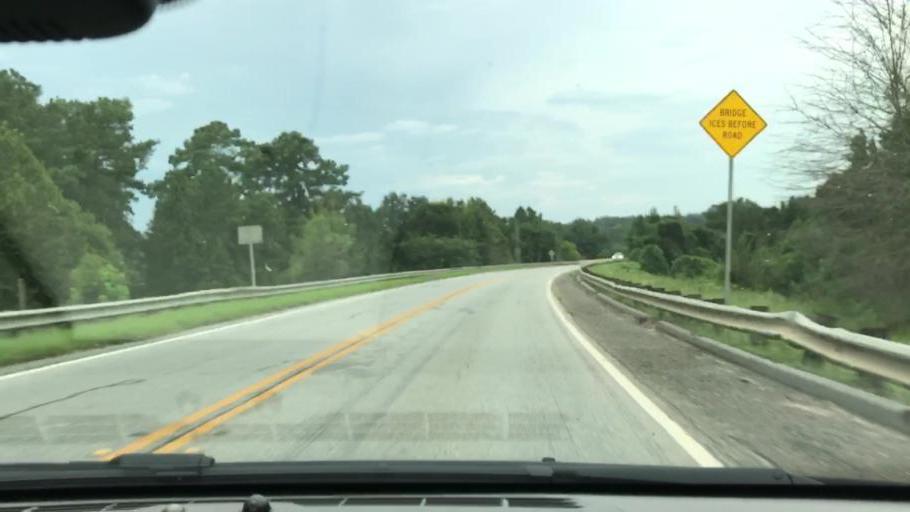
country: US
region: Alabama
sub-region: Houston County
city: Ashford
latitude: 31.2817
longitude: -85.0980
